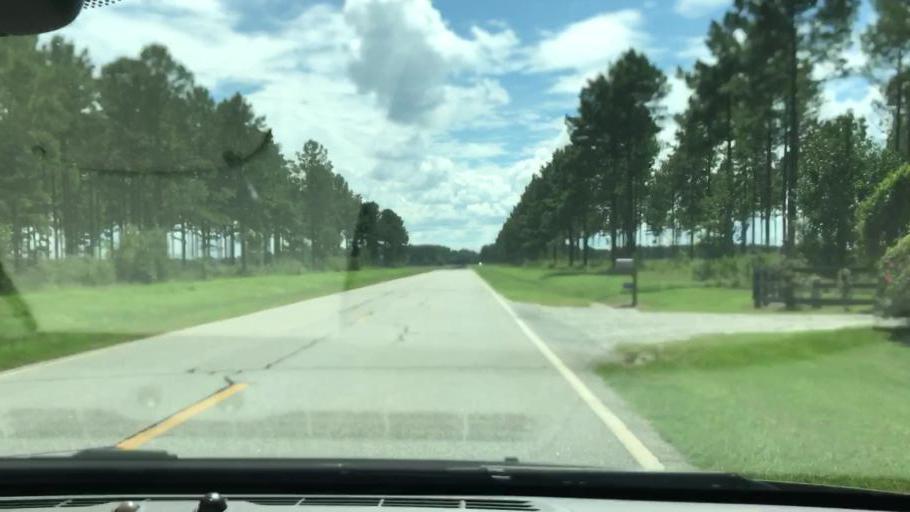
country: US
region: Georgia
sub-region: Quitman County
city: Georgetown
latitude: 32.0596
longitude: -85.0363
